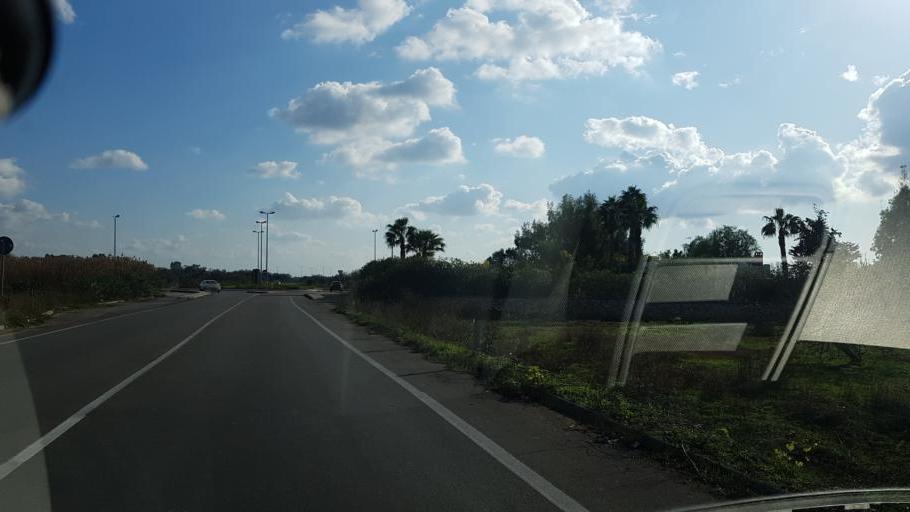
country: IT
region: Apulia
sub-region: Provincia di Lecce
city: Veglie
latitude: 40.3399
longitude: 17.9794
